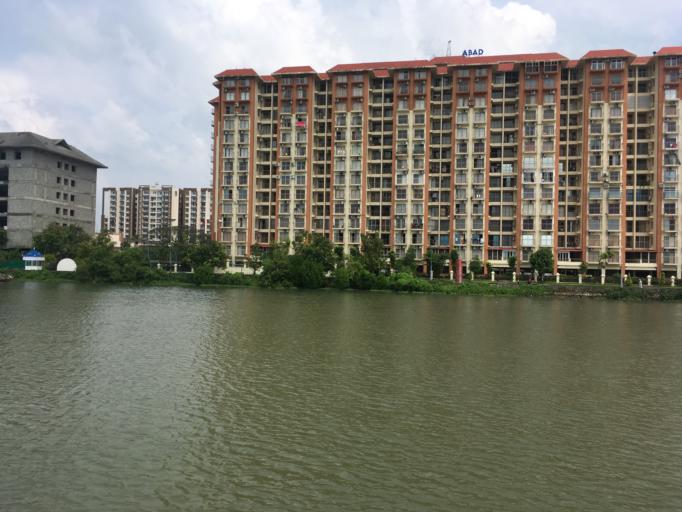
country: IN
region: Kerala
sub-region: Ernakulam
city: Cochin
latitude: 9.9871
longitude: 76.2703
